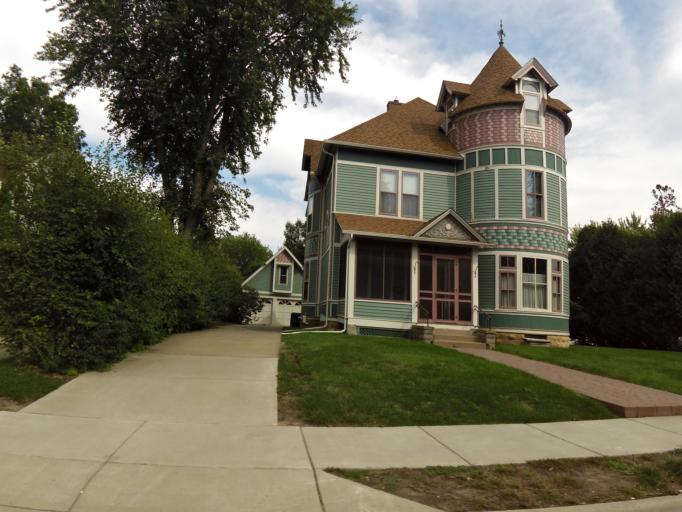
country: US
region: Minnesota
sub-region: Washington County
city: Stillwater
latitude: 45.0492
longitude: -92.8063
